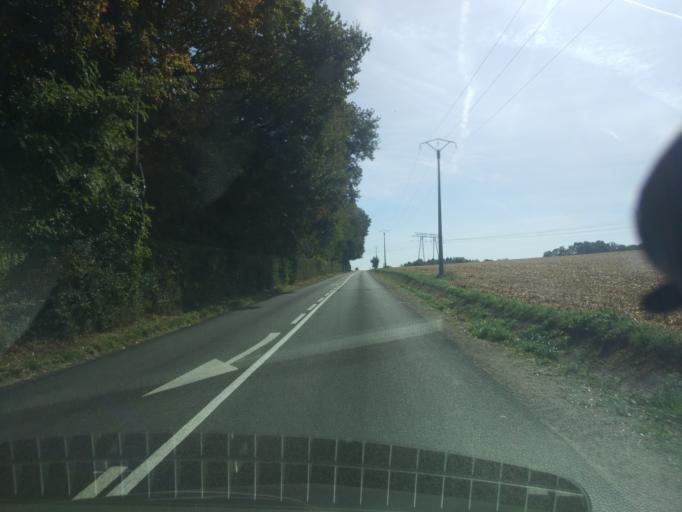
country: FR
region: Ile-de-France
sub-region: Departement de l'Essonne
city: Forges-les-Bains
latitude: 48.6393
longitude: 2.1016
